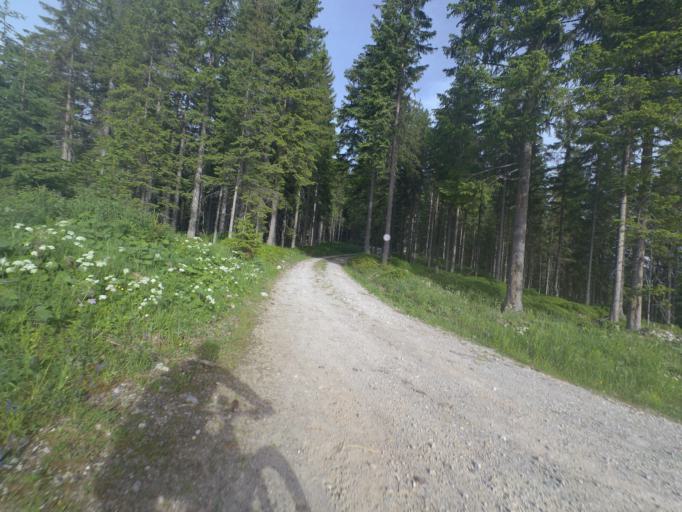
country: AT
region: Salzburg
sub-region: Politischer Bezirk Sankt Johann im Pongau
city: Muhlbach am Hochkonig
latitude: 47.3646
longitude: 13.1034
